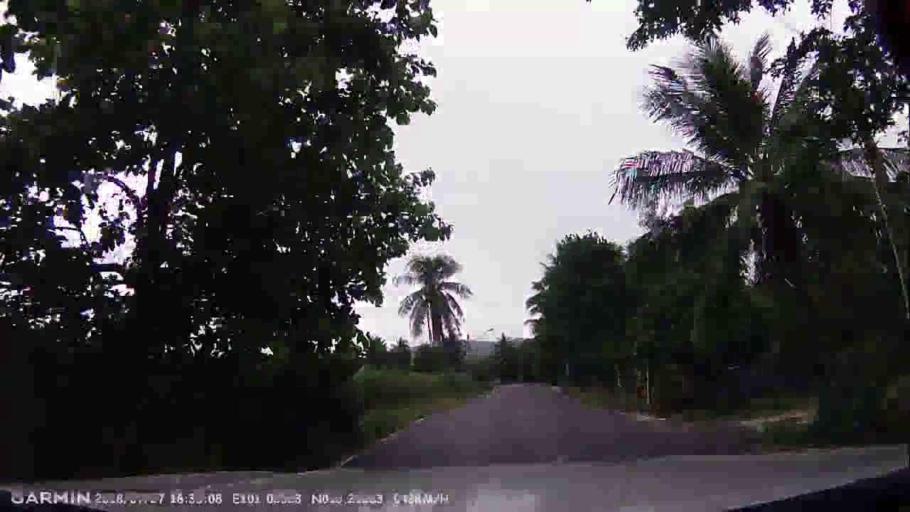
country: TH
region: Chon Buri
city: Si Racha
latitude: 13.2129
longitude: 101.0253
